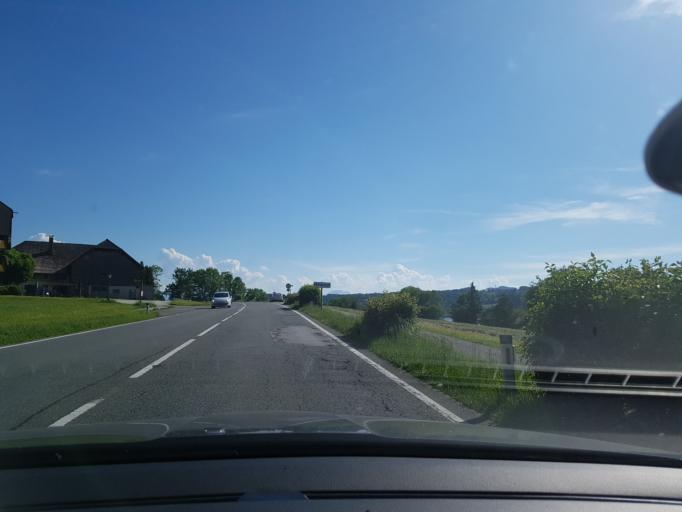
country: AT
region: Salzburg
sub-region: Politischer Bezirk Salzburg-Umgebung
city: Seeham
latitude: 47.9512
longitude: 13.0891
